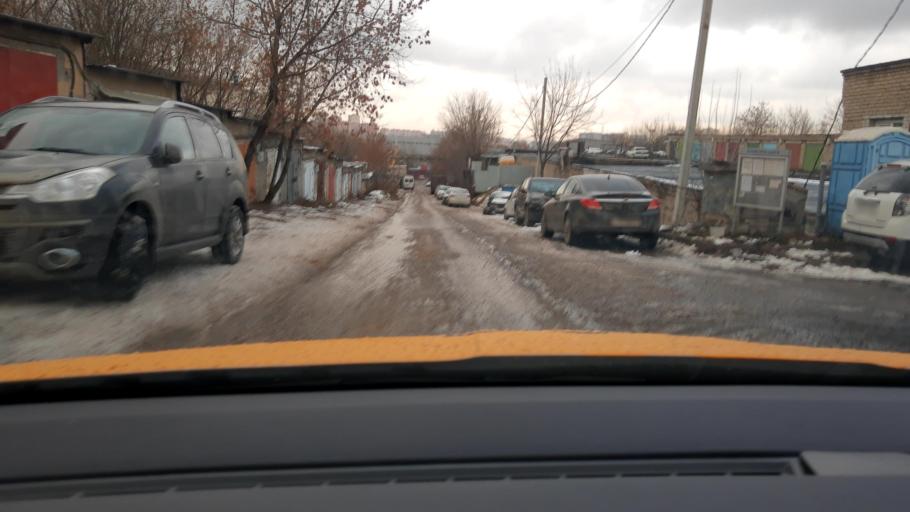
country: RU
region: Moskovskaya
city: Kotel'niki
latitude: 55.6431
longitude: 37.8339
